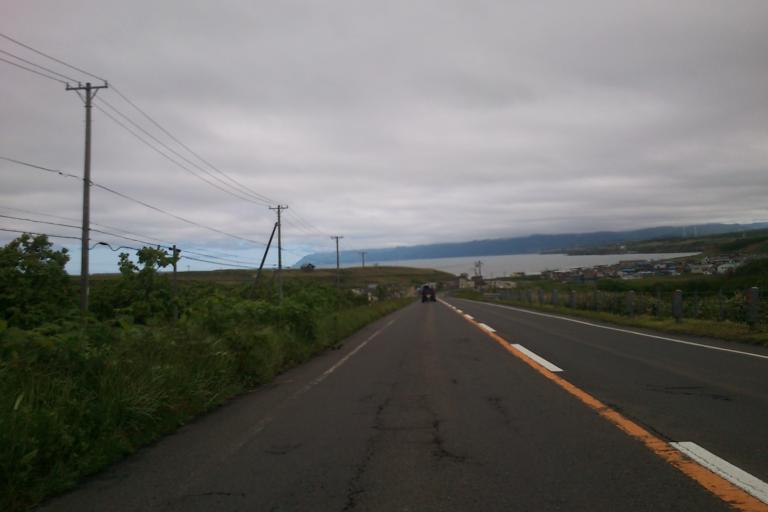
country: JP
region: Hokkaido
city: Ishikari
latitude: 43.3068
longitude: 141.4123
